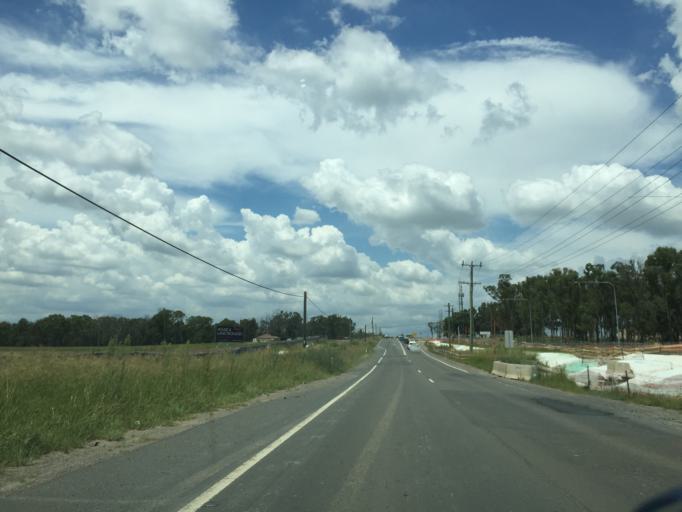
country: AU
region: New South Wales
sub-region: Blacktown
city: Hassall Grove
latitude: -33.7094
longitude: 150.8406
